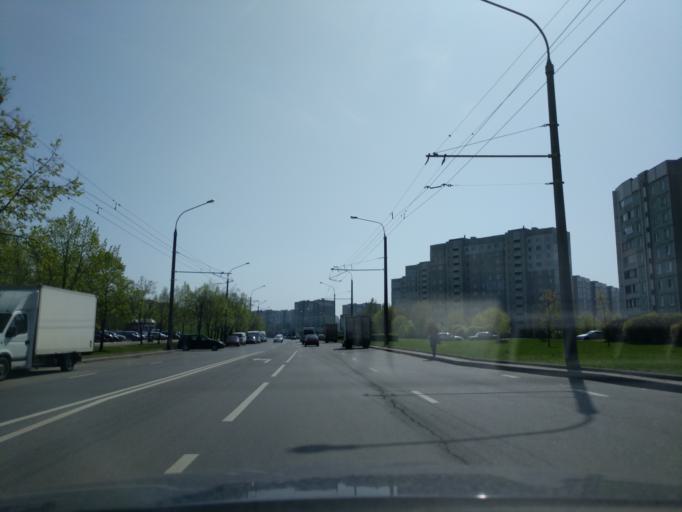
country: BY
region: Minsk
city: Malinovka
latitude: 53.8623
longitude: 27.4580
